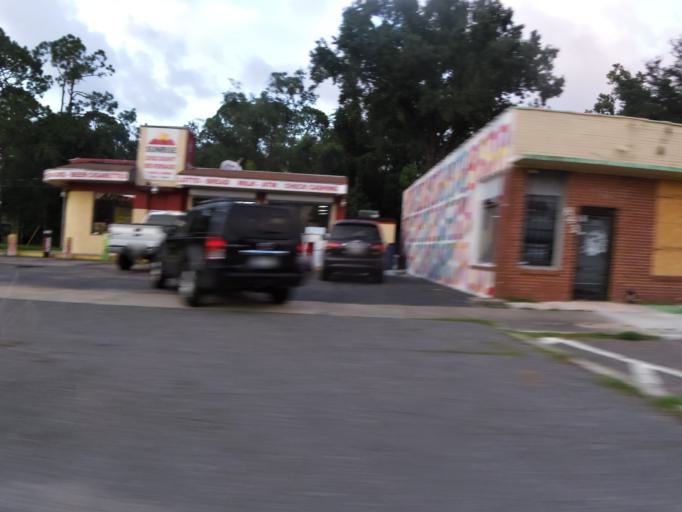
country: US
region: Florida
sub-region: Duval County
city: Jacksonville
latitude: 30.3139
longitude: -81.7199
